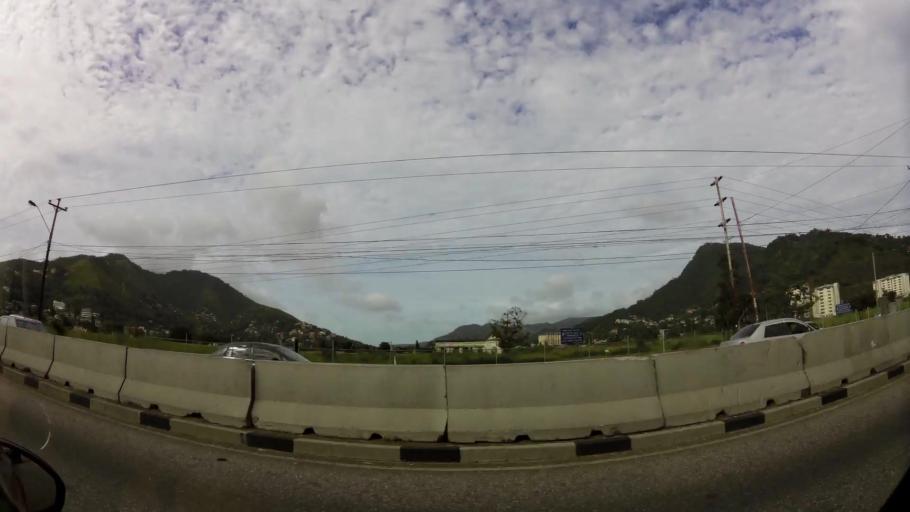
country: TT
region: City of Port of Spain
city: Mucurapo
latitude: 10.6796
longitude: -61.5559
